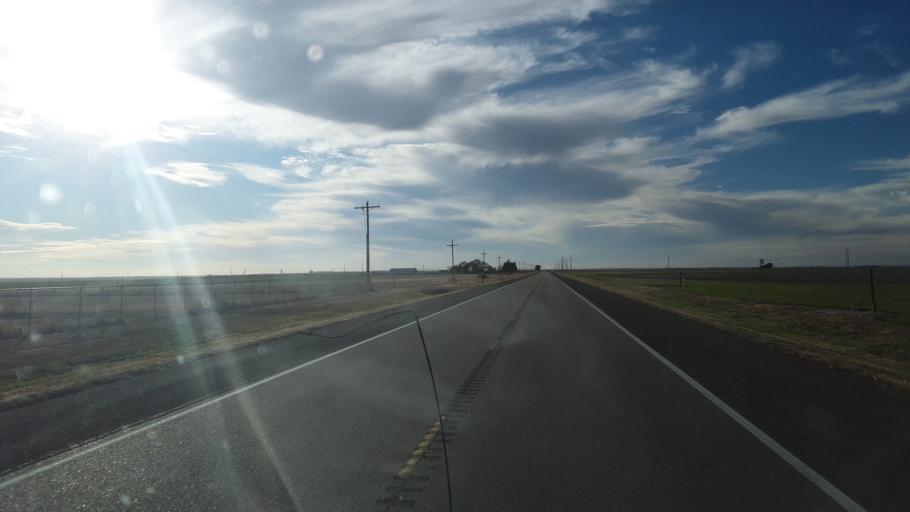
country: US
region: Kansas
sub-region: Finney County
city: Holcomb
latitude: 38.0034
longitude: -101.0495
